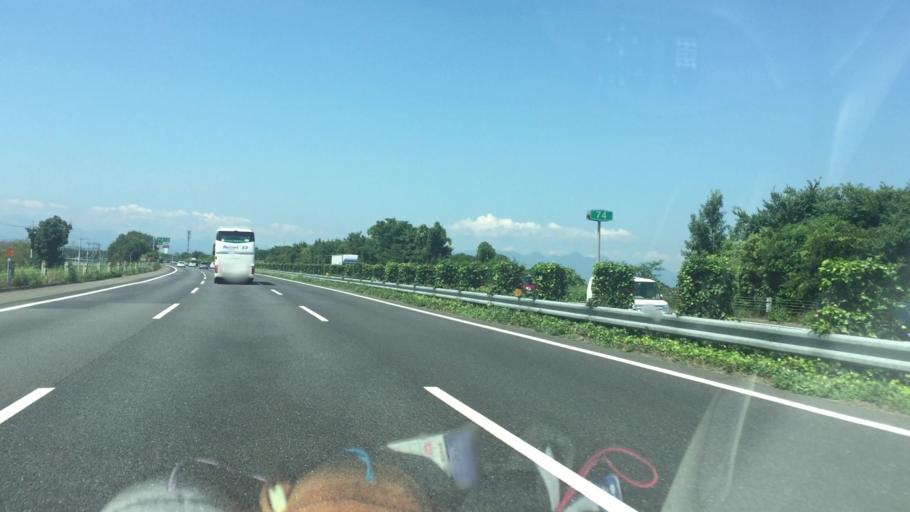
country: JP
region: Gunma
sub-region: Sawa-gun
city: Tamamura
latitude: 36.2496
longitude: 139.1357
